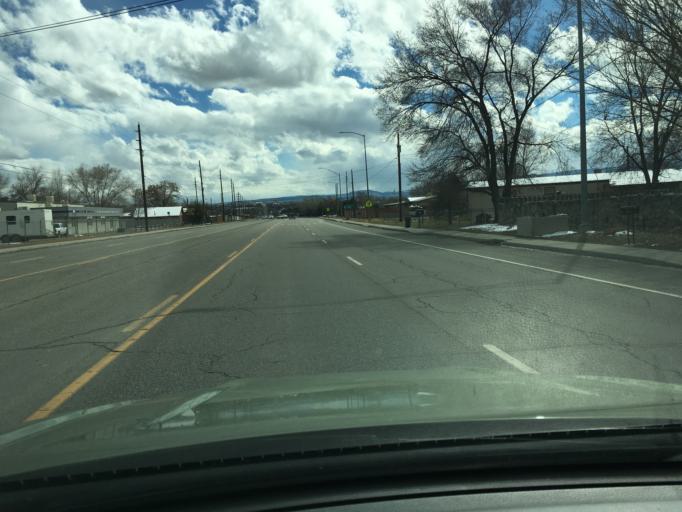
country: US
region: Colorado
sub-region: Mesa County
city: Clifton
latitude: 39.0721
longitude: -108.4594
